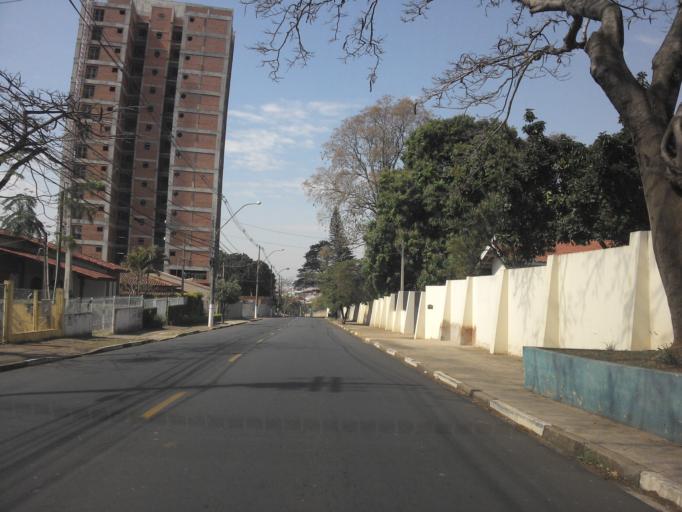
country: BR
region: Sao Paulo
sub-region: Hortolandia
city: Hortolandia
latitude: -22.8778
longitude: -47.2253
